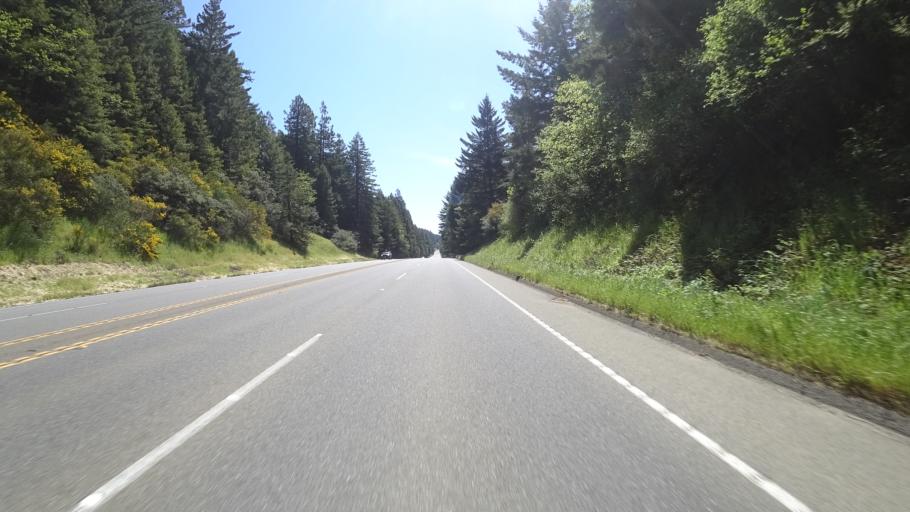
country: US
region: California
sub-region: Humboldt County
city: Westhaven-Moonstone
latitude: 41.0526
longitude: -124.1241
